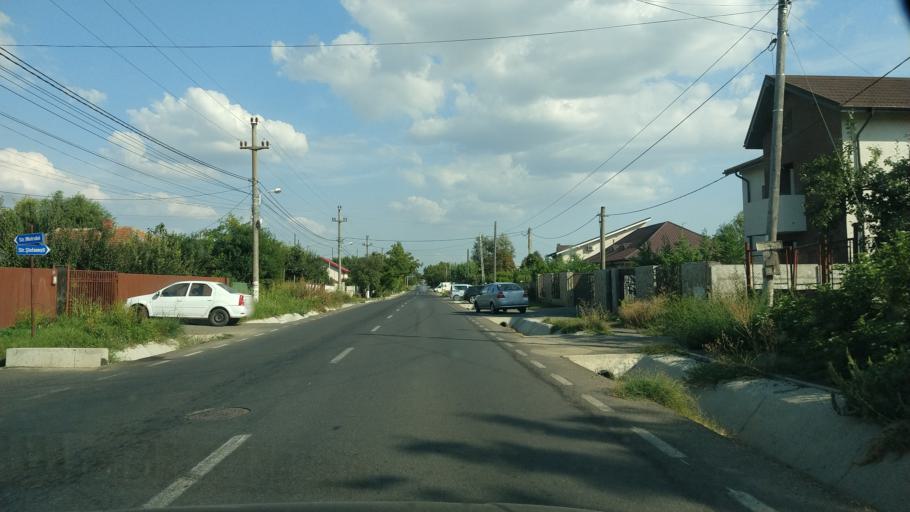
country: RO
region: Ilfov
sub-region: Comuna Afumati
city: Afumati
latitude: 44.5311
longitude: 26.2351
